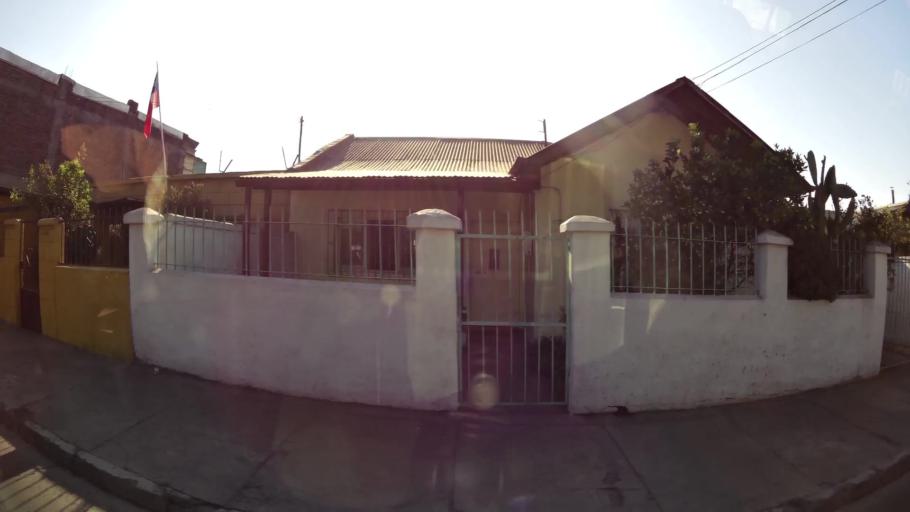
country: CL
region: Santiago Metropolitan
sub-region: Provincia de Santiago
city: Santiago
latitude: -33.3884
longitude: -70.6709
